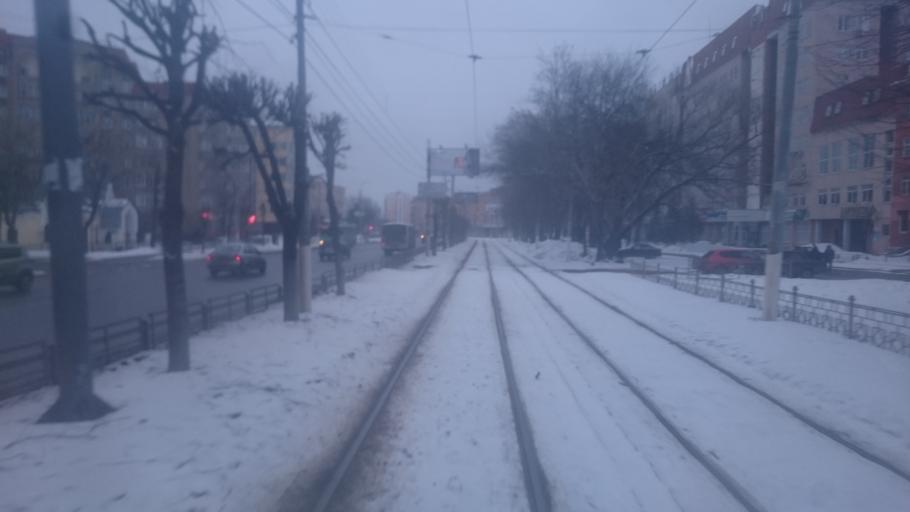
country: RU
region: Tverskaya
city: Tver
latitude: 56.8446
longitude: 35.9032
